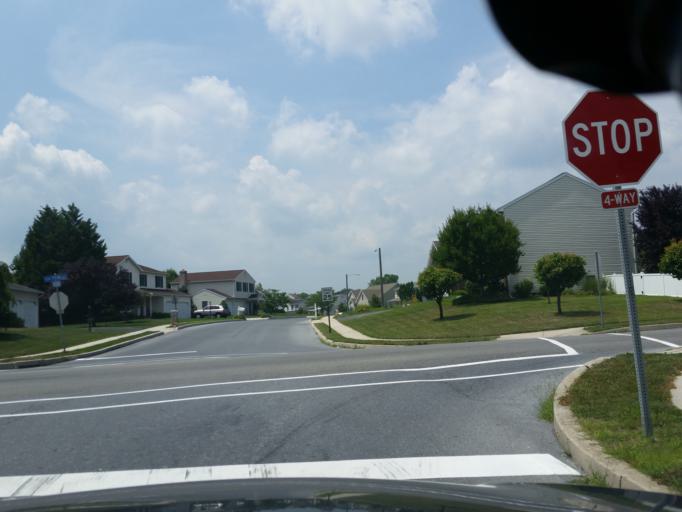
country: US
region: Pennsylvania
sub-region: Cumberland County
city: Enola
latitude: 40.2949
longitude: -76.9489
